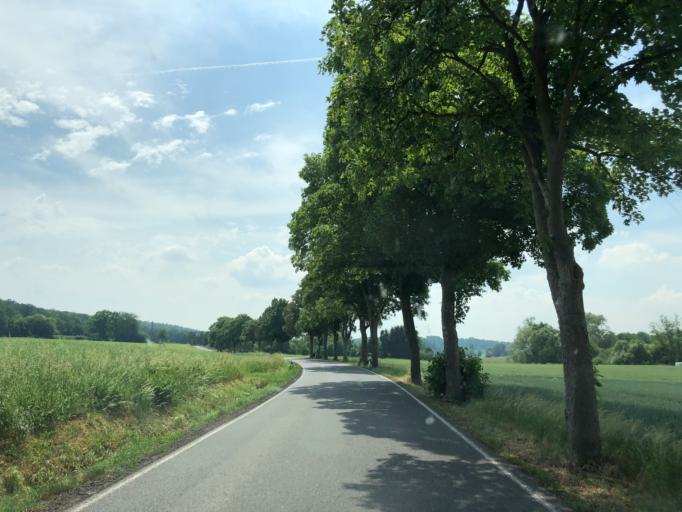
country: DE
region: Hesse
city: Schwalmstadt
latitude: 50.9418
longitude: 9.2018
